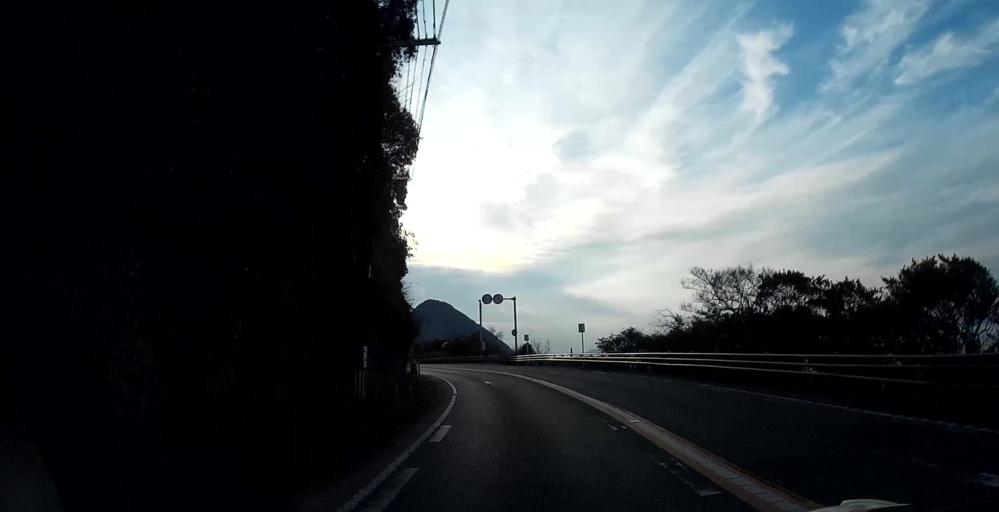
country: JP
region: Nagasaki
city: Shimabara
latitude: 32.6332
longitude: 130.4611
